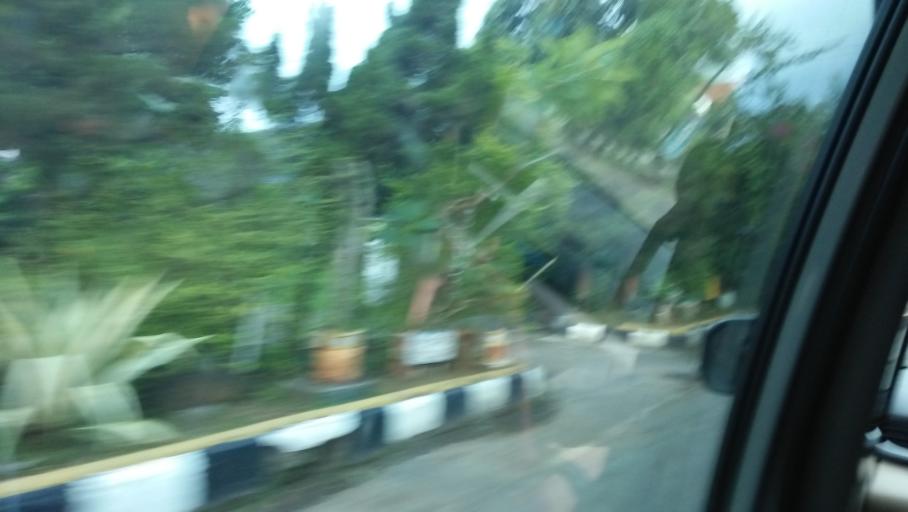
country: ID
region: Central Java
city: Mlonggo
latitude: -6.5956
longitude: 110.6760
